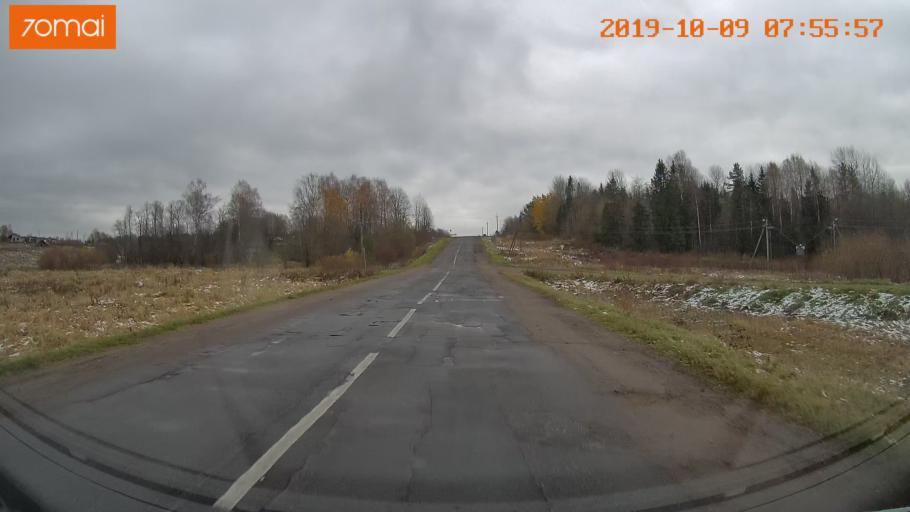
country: RU
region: Jaroslavl
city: Kukoboy
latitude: 58.6988
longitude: 39.9287
